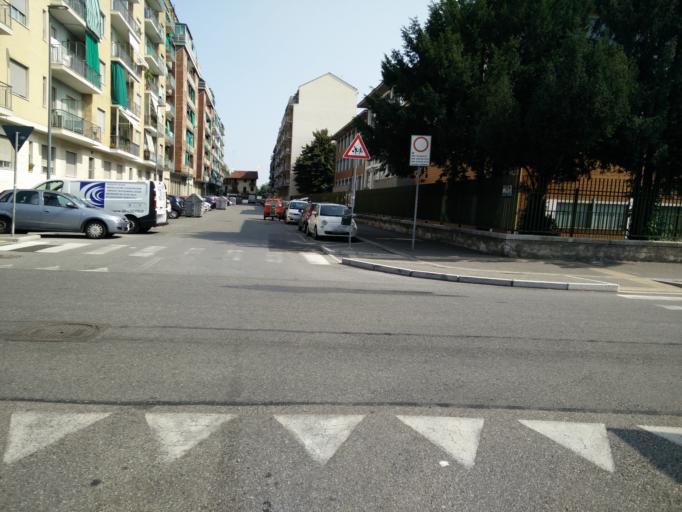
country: IT
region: Piedmont
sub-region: Provincia di Torino
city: Nichelino
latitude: 45.0226
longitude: 7.6536
